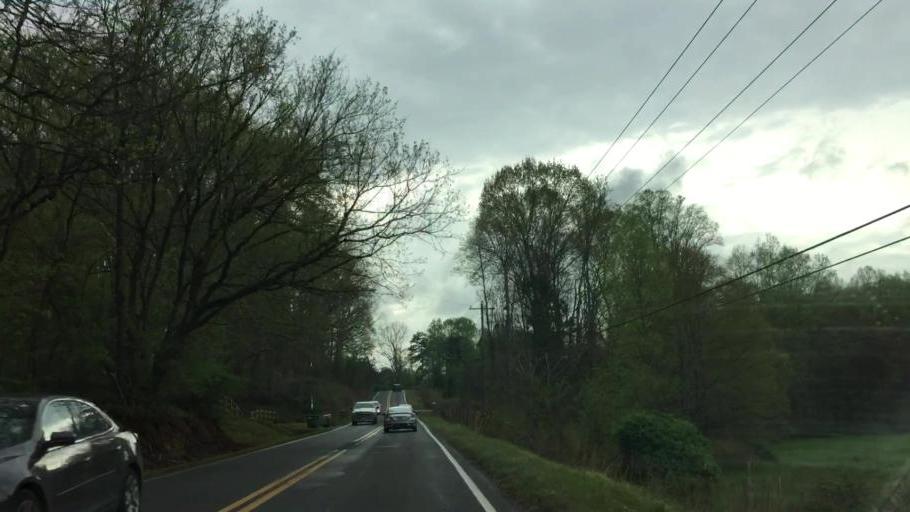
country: US
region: Georgia
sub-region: Fulton County
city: Milton
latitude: 34.1993
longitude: -84.3689
